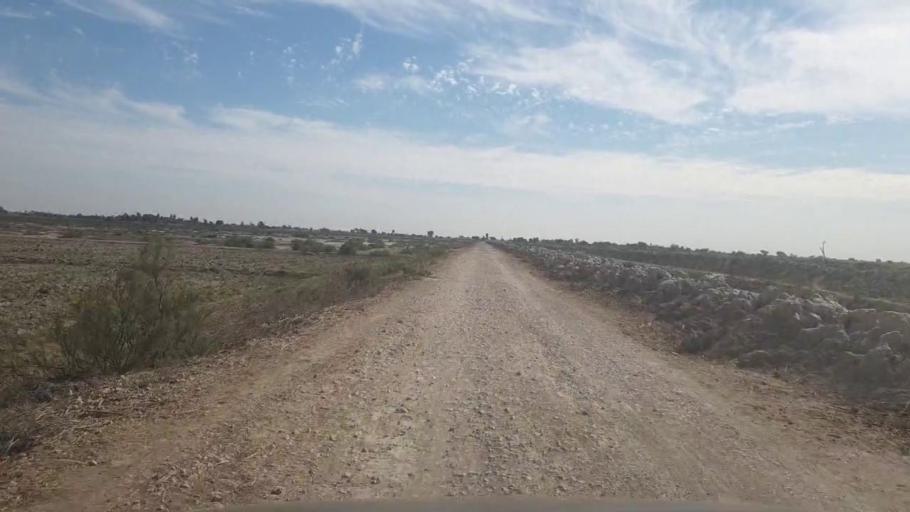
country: PK
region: Sindh
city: Mirwah Gorchani
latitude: 25.4268
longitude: 69.2004
